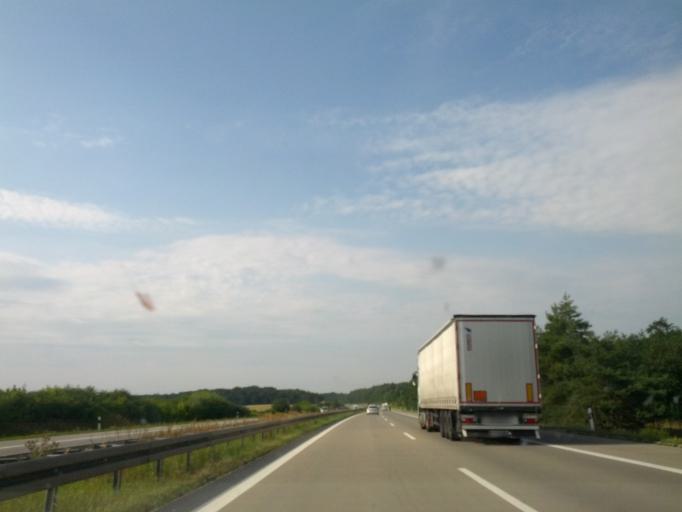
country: DE
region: Mecklenburg-Vorpommern
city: Dummerstorf
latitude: 53.9153
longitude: 12.2372
